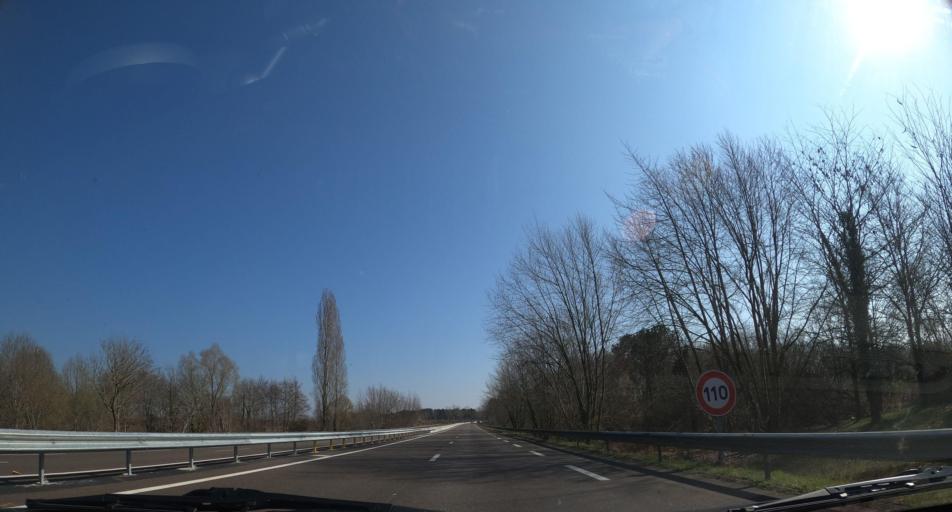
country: FR
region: Aquitaine
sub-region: Departement des Landes
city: Saint-Perdon
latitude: 43.8673
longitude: -0.6347
